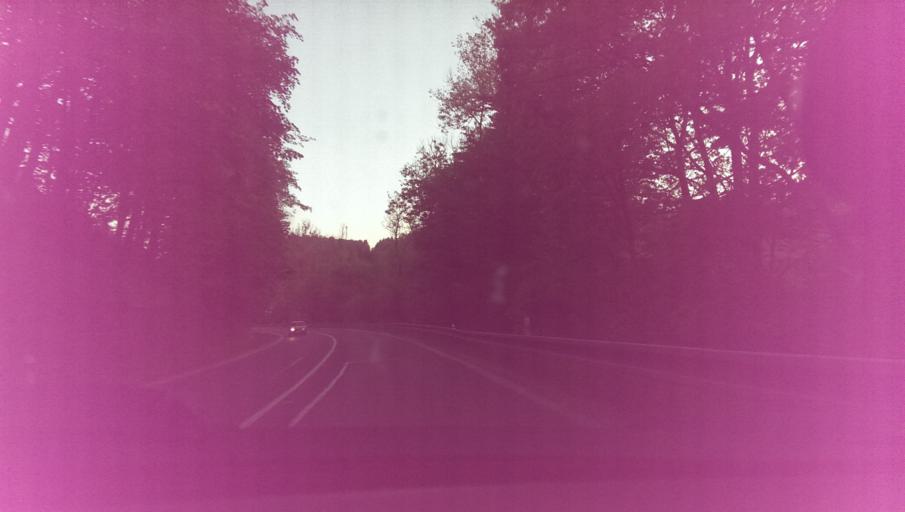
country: CZ
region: Zlin
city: Valasske Mezirici
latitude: 49.4297
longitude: 17.9574
